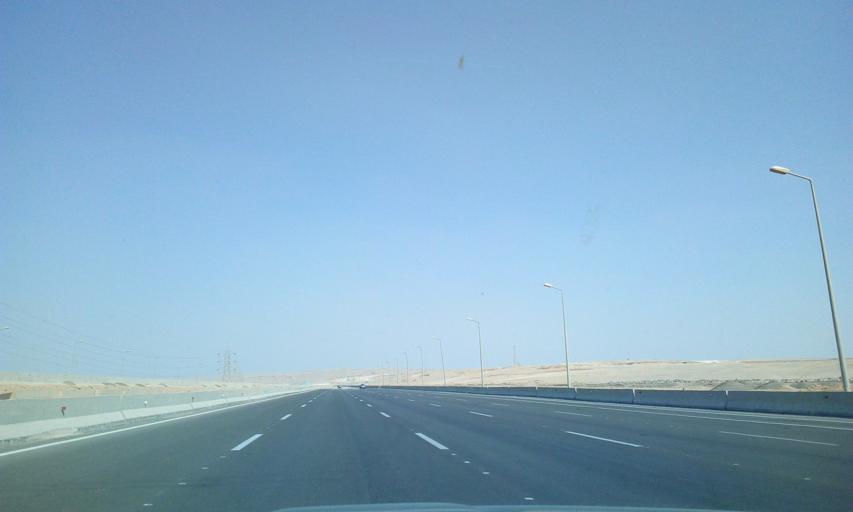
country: EG
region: As Suways
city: Ain Sukhna
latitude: 29.7627
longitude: 31.9654
